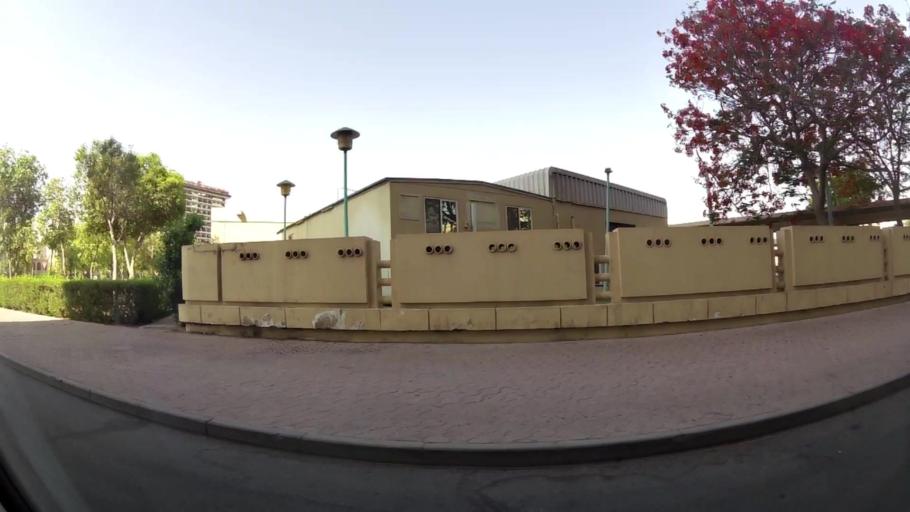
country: AE
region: Ash Shariqah
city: Sharjah
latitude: 25.2664
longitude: 55.2941
